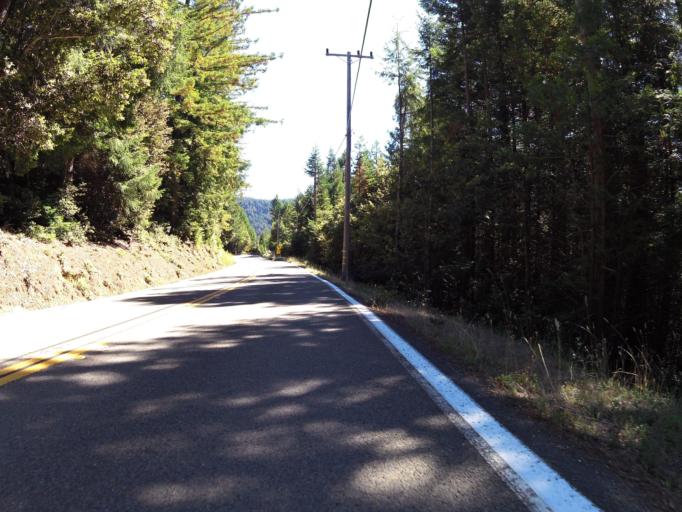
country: US
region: California
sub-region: Mendocino County
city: Fort Bragg
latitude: 39.7216
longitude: -123.8068
